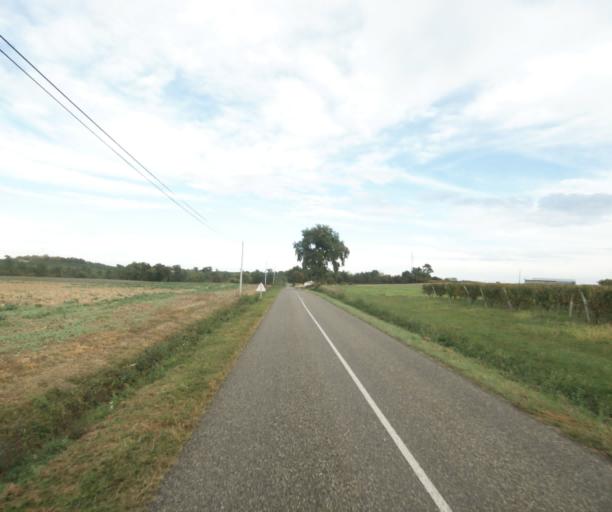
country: FR
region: Midi-Pyrenees
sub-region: Departement du Gers
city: Le Houga
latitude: 43.8554
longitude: -0.1387
